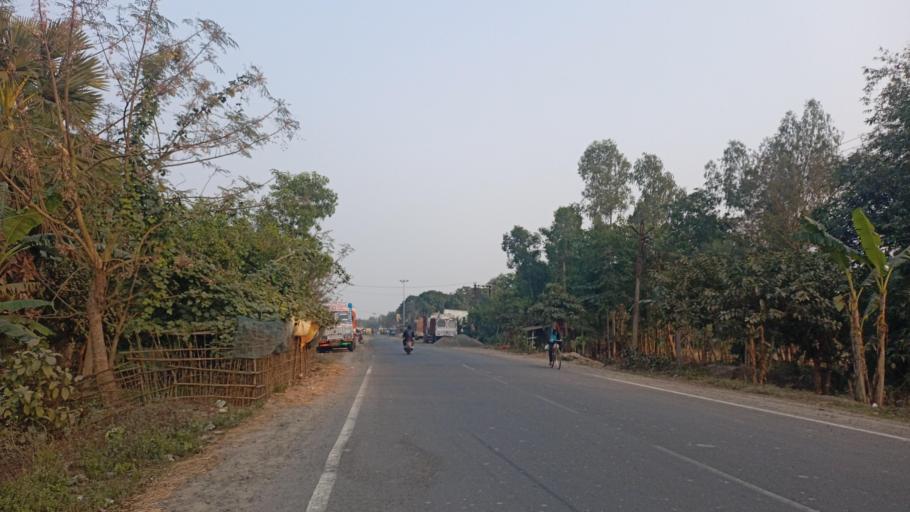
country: IN
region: West Bengal
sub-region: Dakshin Dinajpur
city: Balurghat
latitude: 25.3130
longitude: 88.8896
